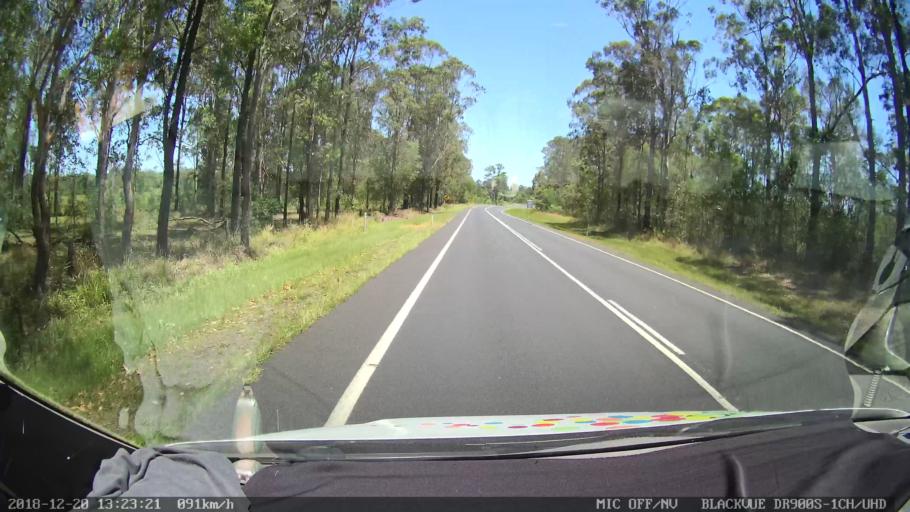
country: AU
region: New South Wales
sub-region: Richmond Valley
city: Casino
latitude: -29.1034
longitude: 153.0002
